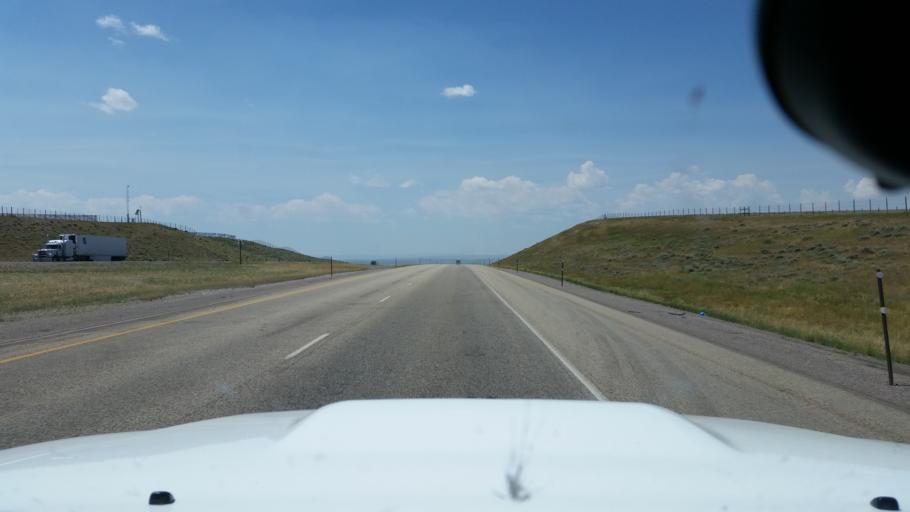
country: US
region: Wyoming
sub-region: Carbon County
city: Saratoga
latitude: 41.7344
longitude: -106.6450
